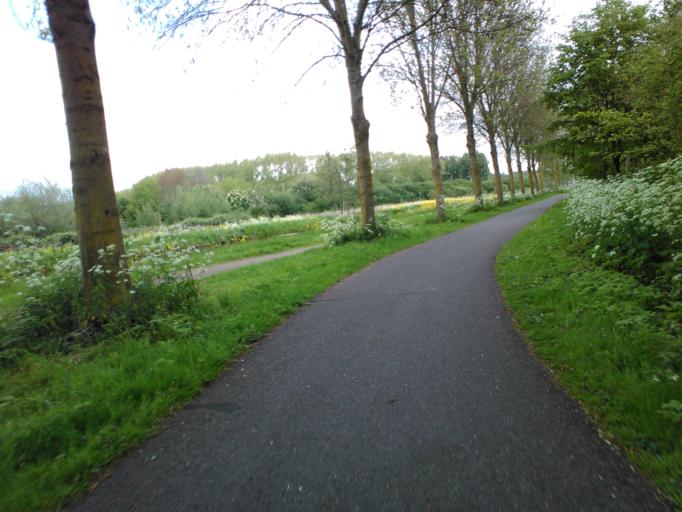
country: NL
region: South Holland
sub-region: Bodegraven-Reeuwijk
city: Reeuwijk
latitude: 52.0548
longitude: 4.7302
